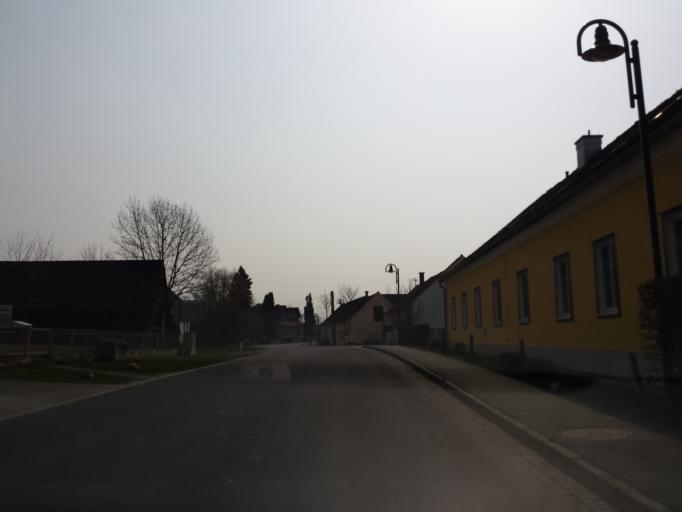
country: AT
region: Styria
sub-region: Politischer Bezirk Hartberg-Fuerstenfeld
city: Loipersdorf bei Fuerstenfeld
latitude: 47.0183
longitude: 16.1044
